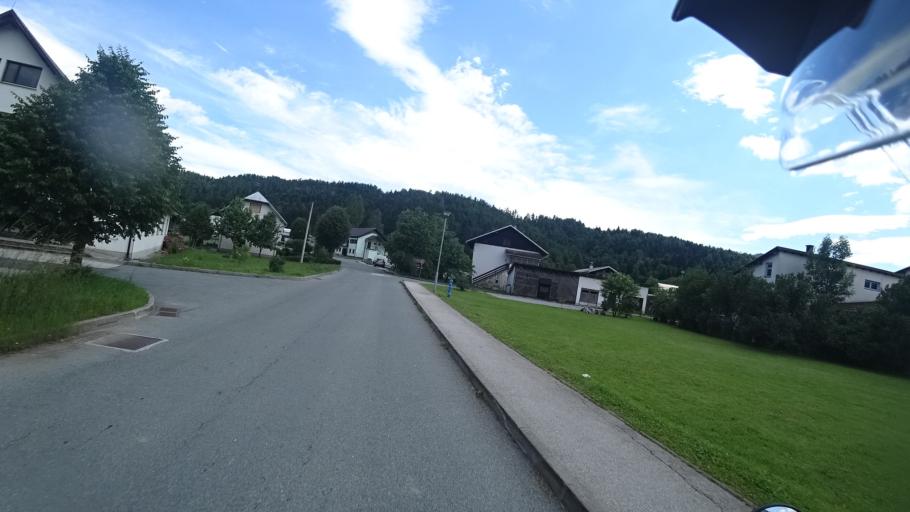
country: SI
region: Osilnica
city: Osilnica
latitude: 45.5155
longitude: 14.6443
